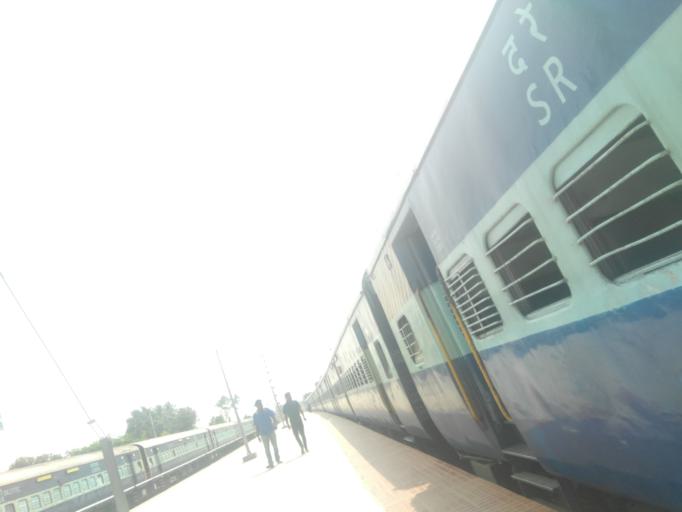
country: IN
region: Tamil Nadu
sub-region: Coimbatore
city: Mettupalayam
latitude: 11.2954
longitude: 76.9363
